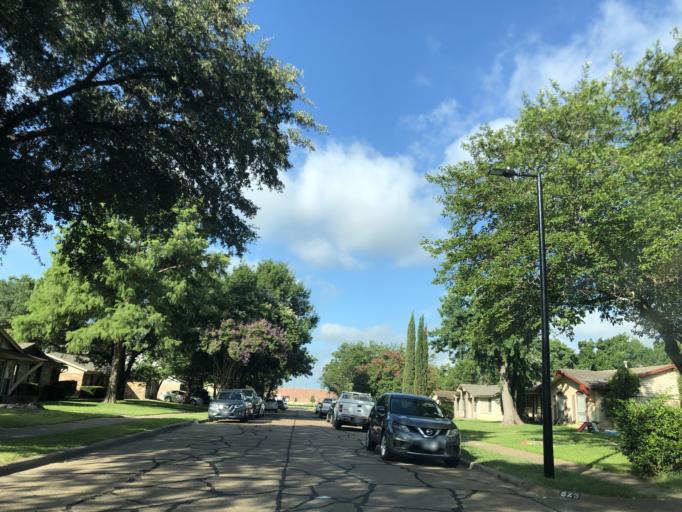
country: US
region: Texas
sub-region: Dallas County
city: Garland
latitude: 32.8574
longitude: -96.6407
